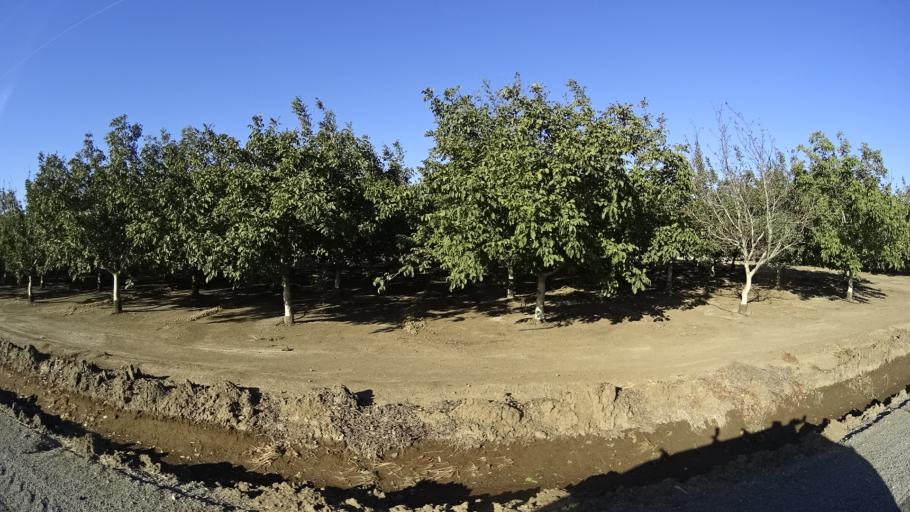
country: US
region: California
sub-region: Yolo County
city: Davis
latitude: 38.5812
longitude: -121.7859
